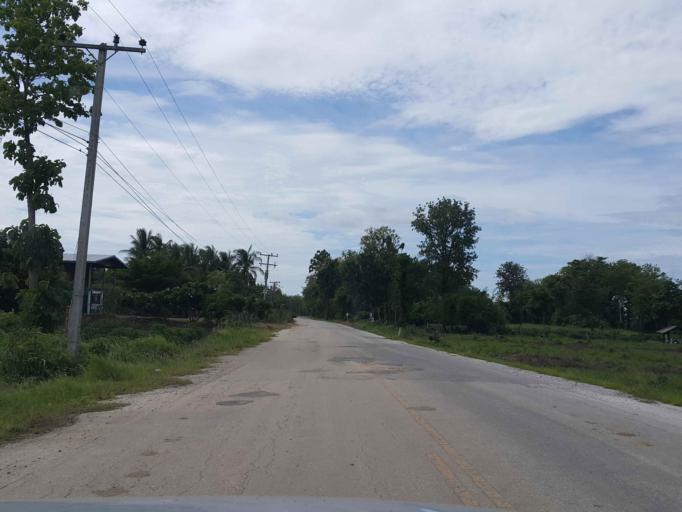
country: TH
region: Sukhothai
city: Ban Dan Lan Hoi
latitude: 17.0865
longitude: 99.4774
